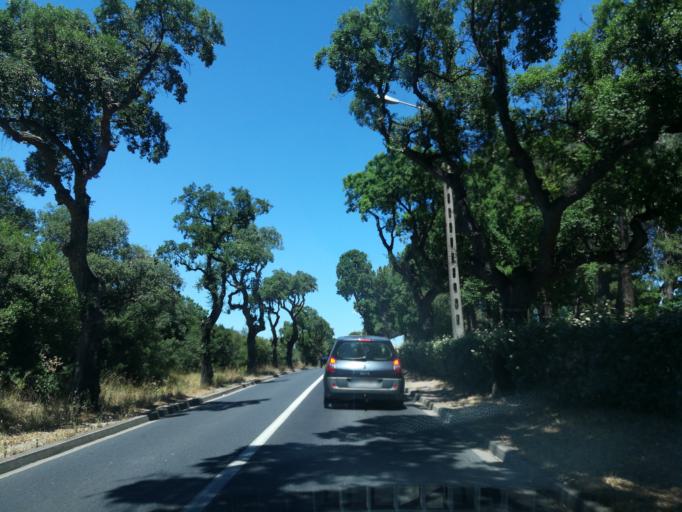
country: FR
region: Languedoc-Roussillon
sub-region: Departement des Pyrenees-Orientales
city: el Volo
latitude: 42.5119
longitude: 2.8291
